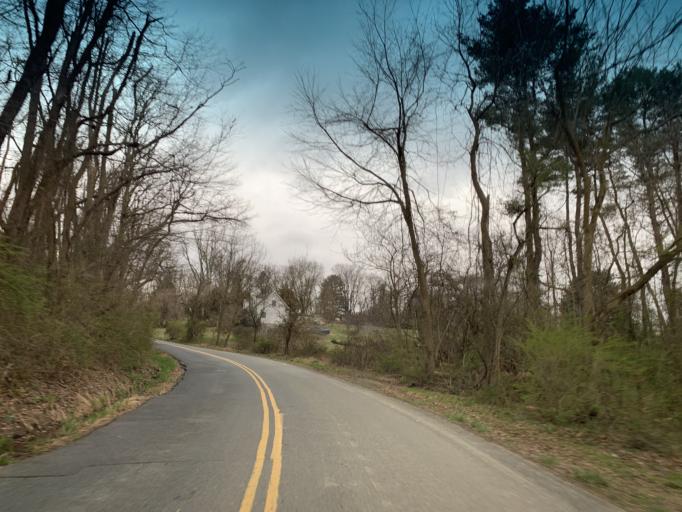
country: US
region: Maryland
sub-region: Harford County
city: Aberdeen
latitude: 39.5393
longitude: -76.1996
